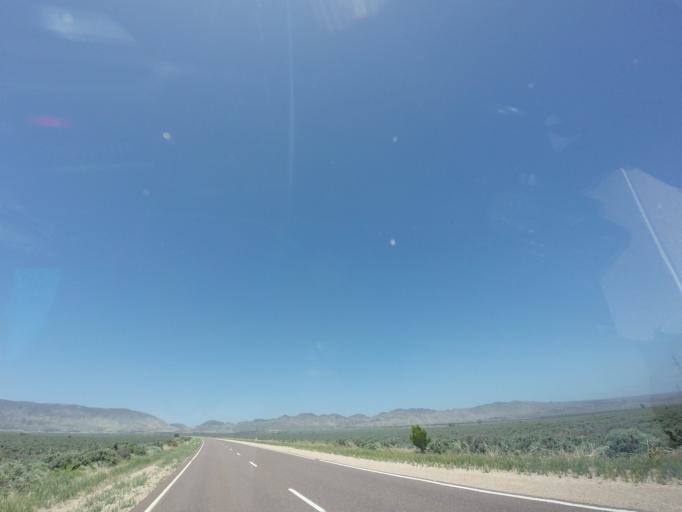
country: AU
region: South Australia
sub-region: Port Augusta
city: Port Augusta
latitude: -32.6258
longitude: 137.9446
